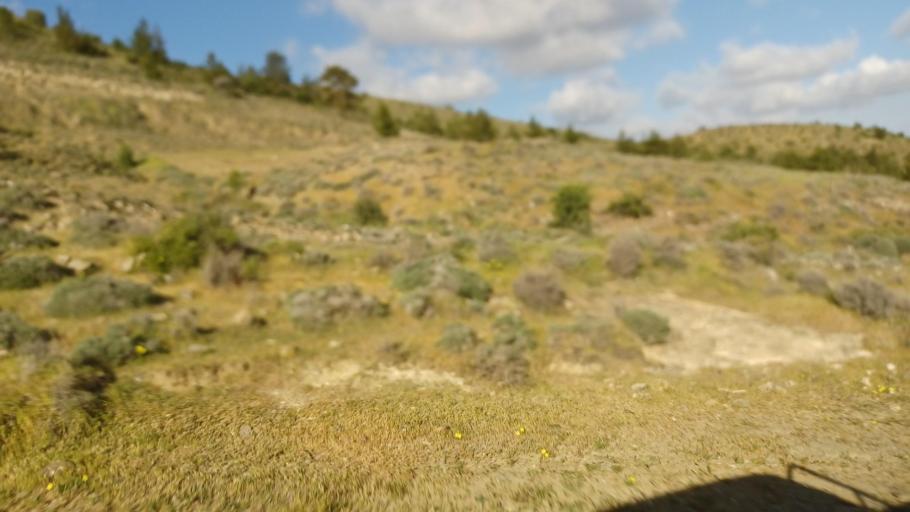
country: CY
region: Lefkosia
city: Peristerona
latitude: 35.0633
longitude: 33.0516
